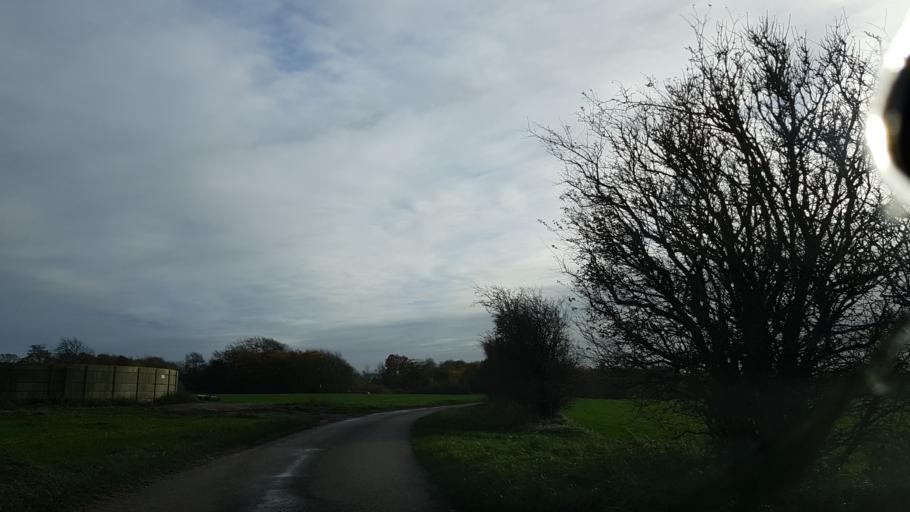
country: DK
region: South Denmark
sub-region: Haderslev Kommune
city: Gram
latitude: 55.2617
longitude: 9.1158
